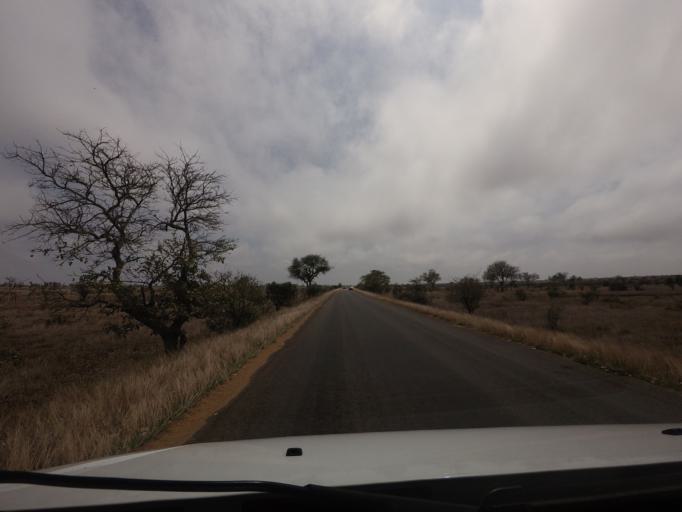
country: ZA
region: Limpopo
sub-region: Mopani District Municipality
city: Phalaborwa
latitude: -24.1951
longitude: 31.7189
